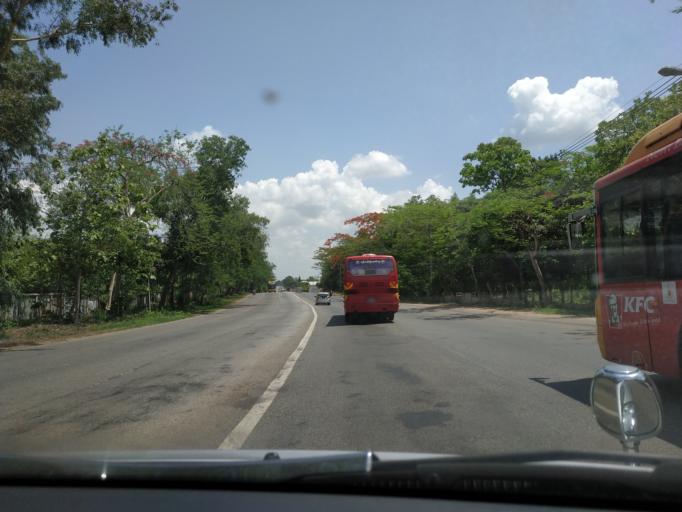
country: MM
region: Yangon
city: Yangon
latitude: 16.9922
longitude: 96.1312
